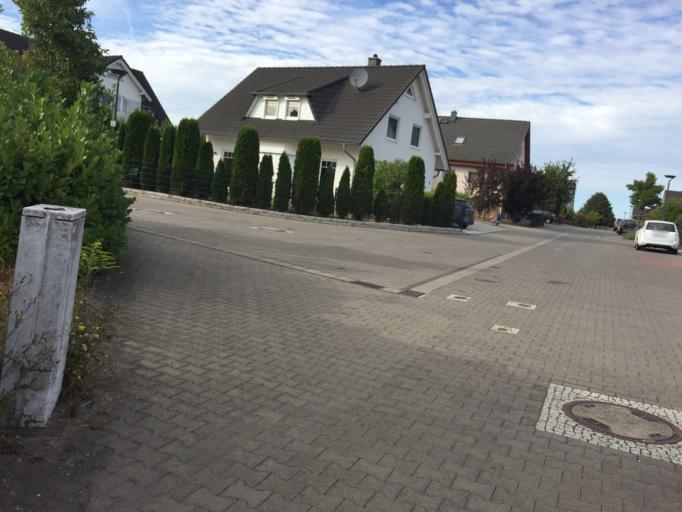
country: DE
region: Hesse
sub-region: Regierungsbezirk Giessen
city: Langgons
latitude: 50.4916
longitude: 8.7243
